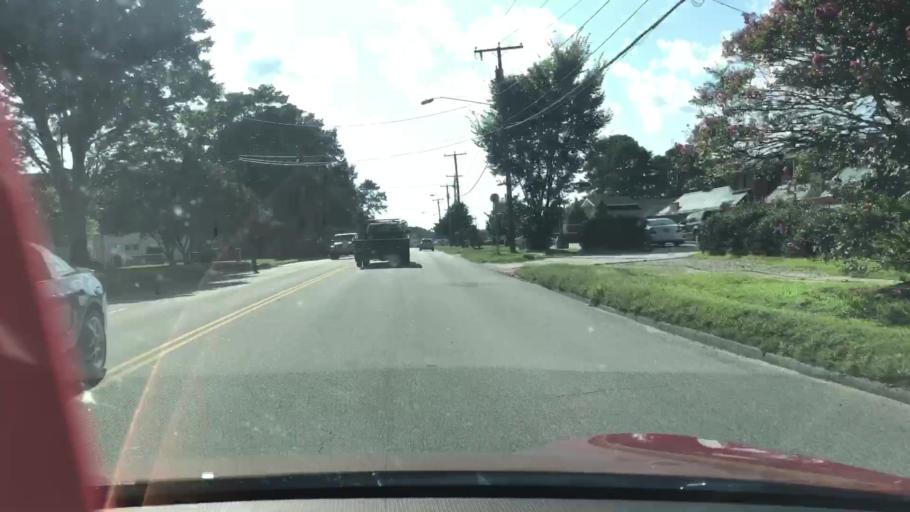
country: US
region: Virginia
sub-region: City of Virginia Beach
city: Virginia Beach
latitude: 36.8424
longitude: -76.0176
